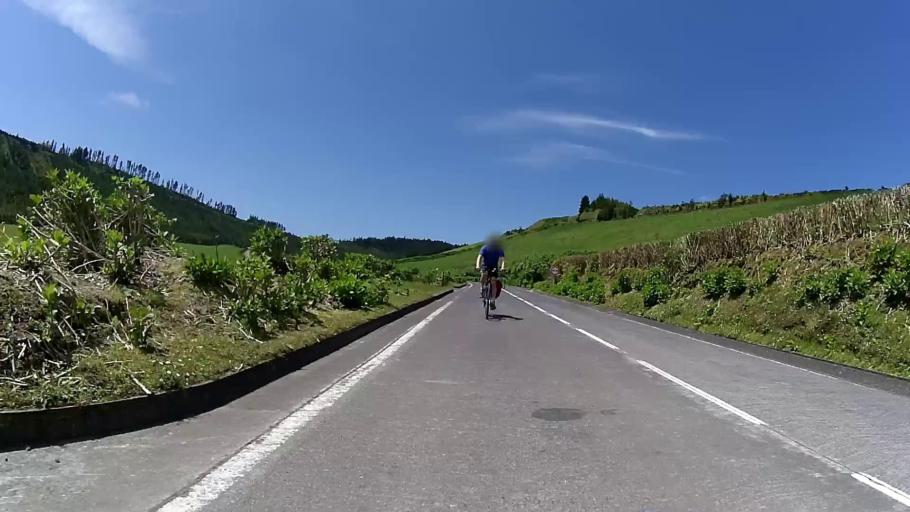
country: PT
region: Azores
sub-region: Ponta Delgada
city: Arrifes
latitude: 37.8413
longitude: -25.7773
